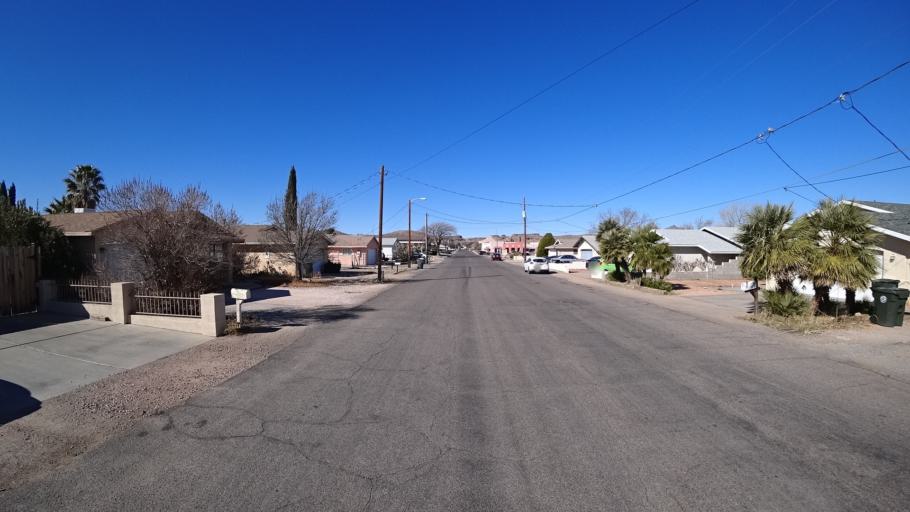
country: US
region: Arizona
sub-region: Mohave County
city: Kingman
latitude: 35.2090
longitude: -114.0329
